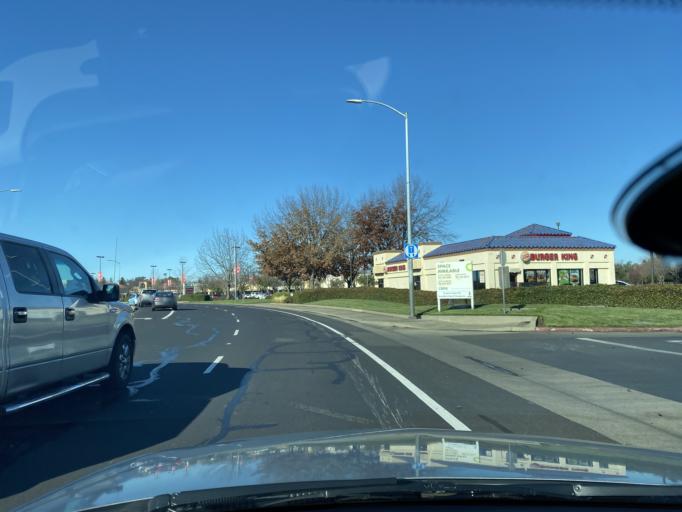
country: US
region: California
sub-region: Sacramento County
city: Elk Grove
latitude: 38.4246
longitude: -121.3904
